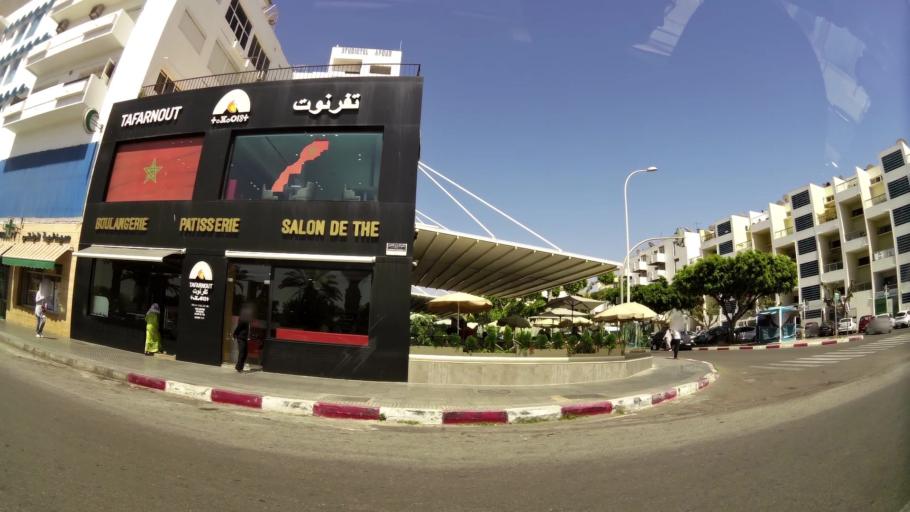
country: MA
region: Souss-Massa-Draa
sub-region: Agadir-Ida-ou-Tnan
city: Agadir
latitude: 30.4173
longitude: -9.5963
